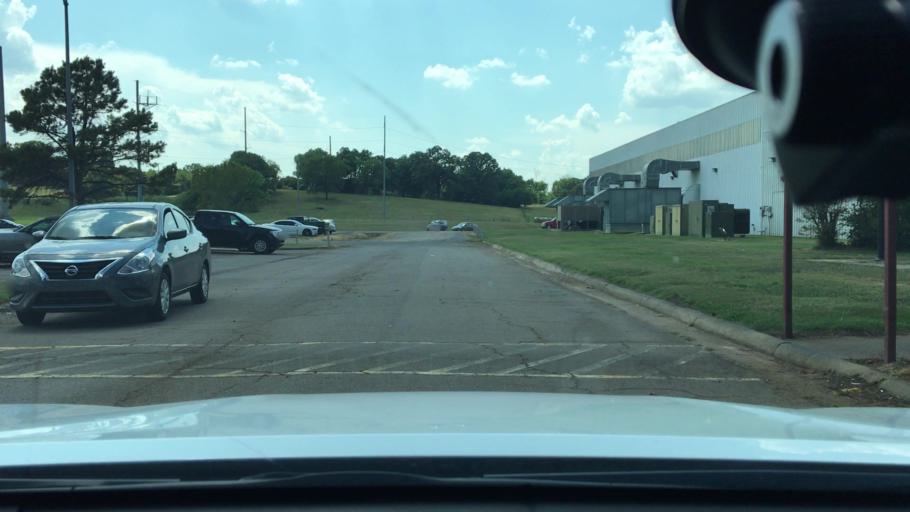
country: US
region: Arkansas
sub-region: Logan County
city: Paris
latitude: 35.2948
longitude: -93.6432
